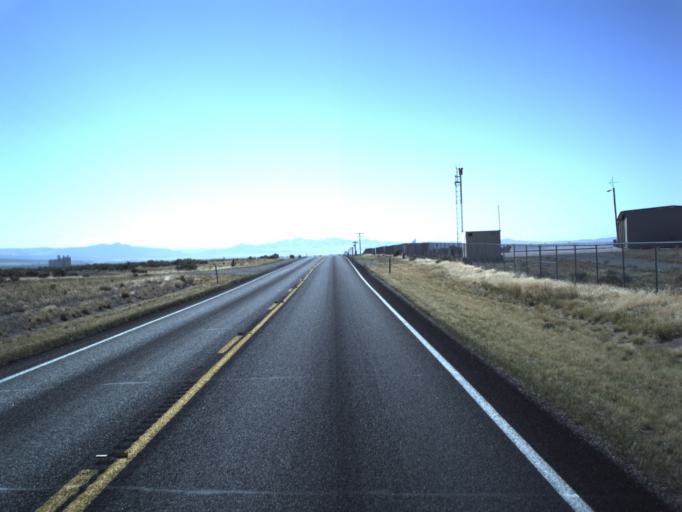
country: US
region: Utah
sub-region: Beaver County
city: Milford
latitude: 38.4204
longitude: -113.0099
